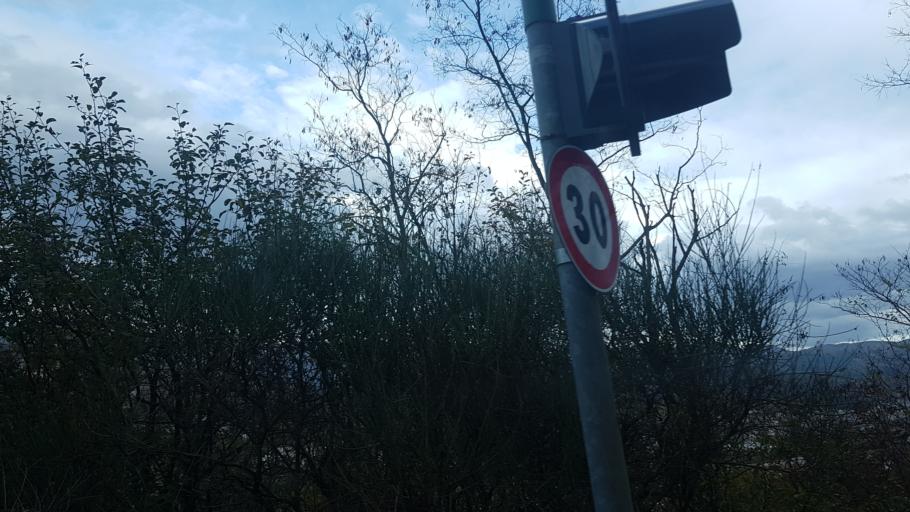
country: IT
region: Abruzzo
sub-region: Provincia dell' Aquila
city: Progetto Case Bazzano
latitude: 42.3633
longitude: 13.4289
